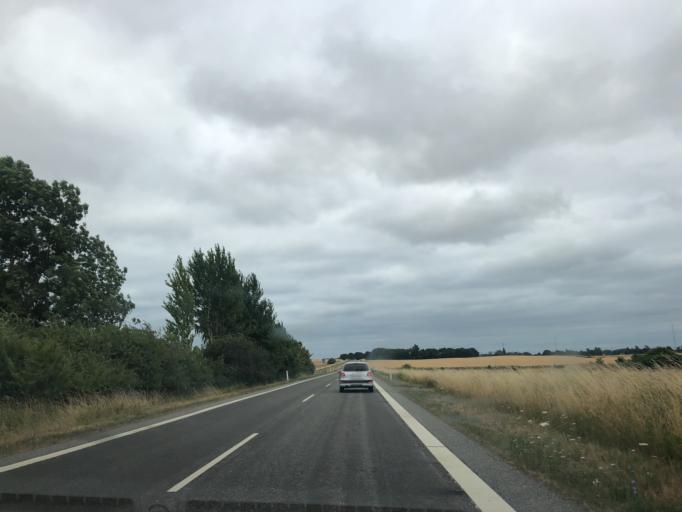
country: DK
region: Zealand
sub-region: Slagelse Kommune
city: Skaelskor
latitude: 55.2292
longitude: 11.3104
